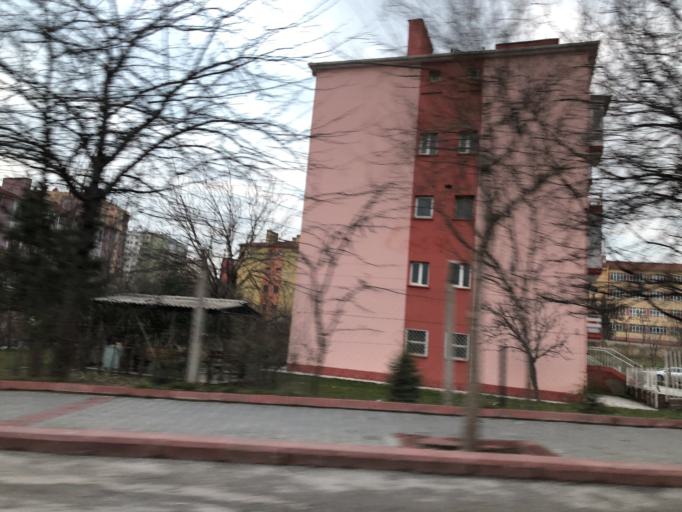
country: TR
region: Ankara
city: Ankara
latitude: 39.9611
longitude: 32.8110
